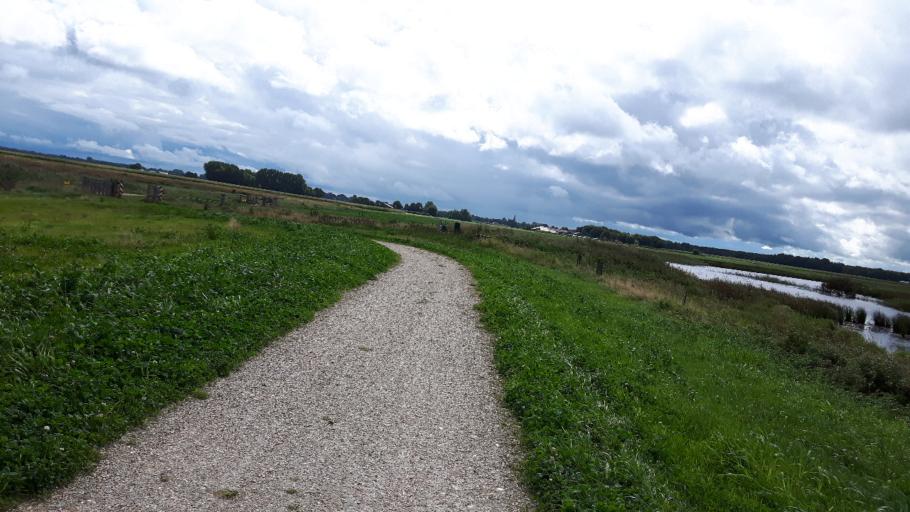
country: NL
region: Groningen
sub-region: Gemeente Slochteren
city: Slochteren
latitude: 53.2571
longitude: 6.7992
